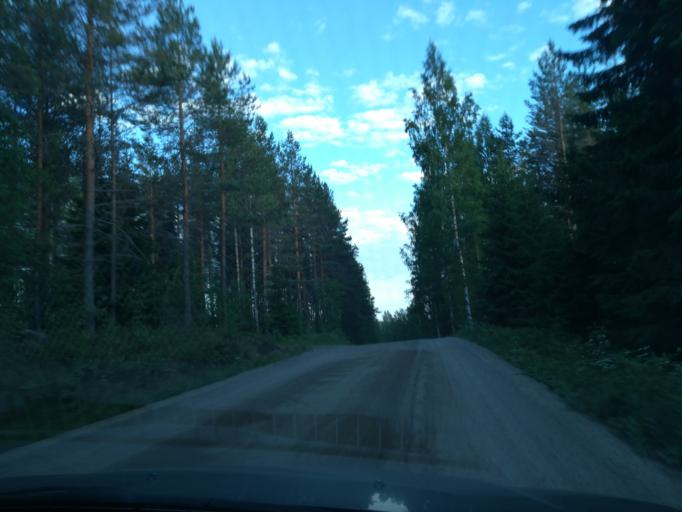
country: FI
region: Southern Savonia
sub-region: Mikkeli
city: Puumala
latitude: 61.5832
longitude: 28.1234
